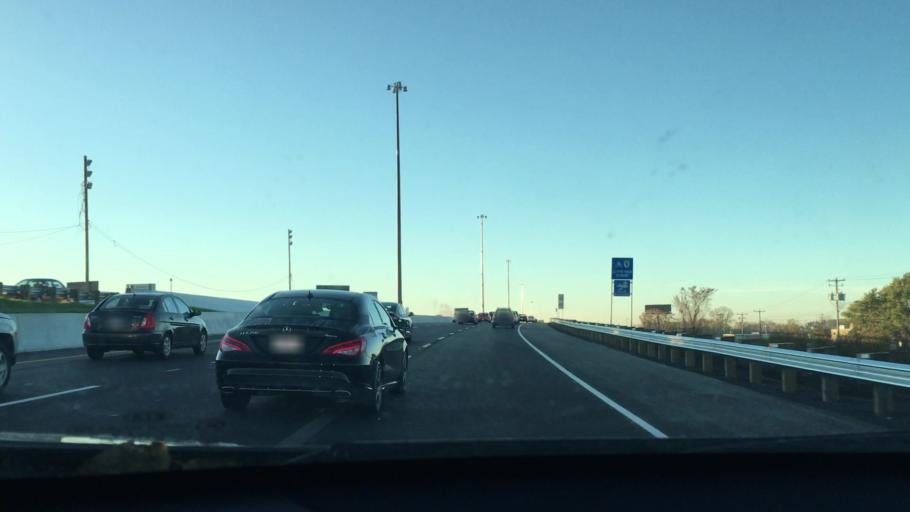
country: CA
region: Quebec
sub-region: Laurentides
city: Saint-Jerome
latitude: 45.7905
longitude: -74.0207
